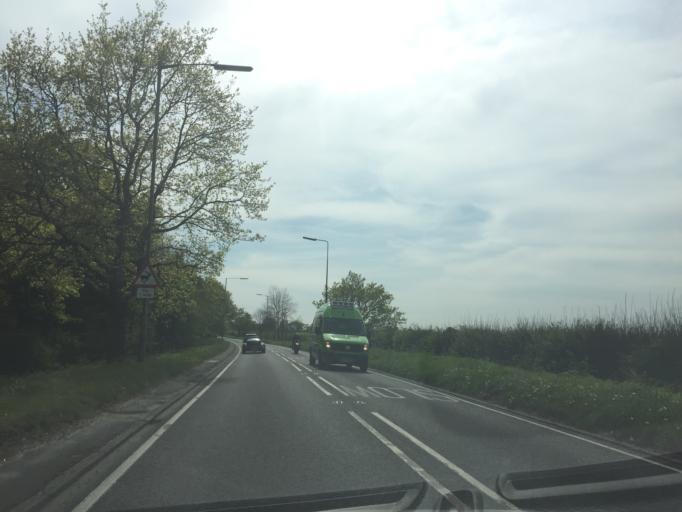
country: GB
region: England
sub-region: Essex
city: Epping
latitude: 51.7179
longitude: 0.1291
